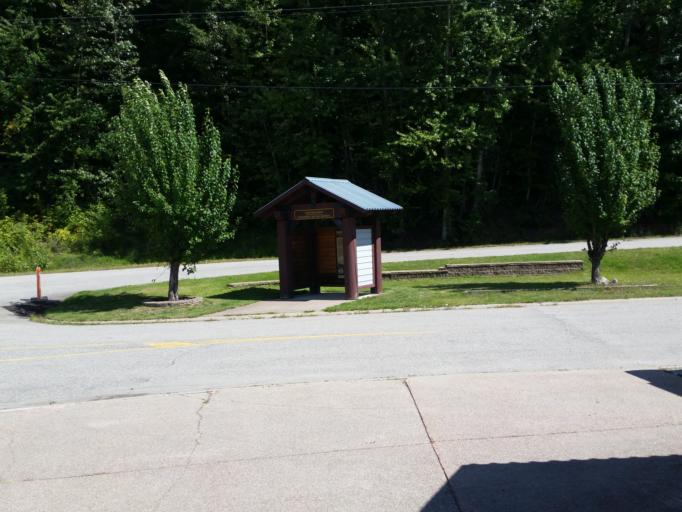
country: CA
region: British Columbia
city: Revelstoke
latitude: 51.0041
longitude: -118.2005
